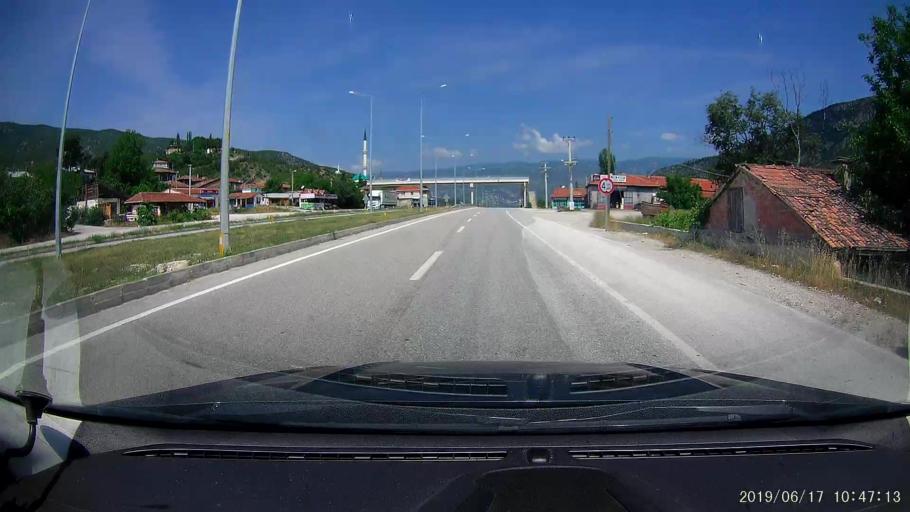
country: TR
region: Corum
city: Hacihamza
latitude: 41.0751
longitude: 34.4522
